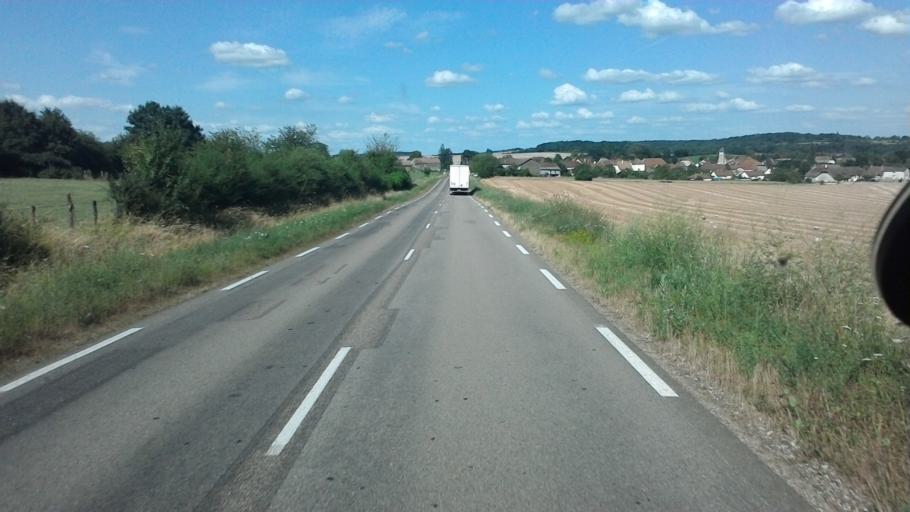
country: FR
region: Franche-Comte
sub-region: Departement de la Haute-Saone
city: Marnay
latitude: 47.3173
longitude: 5.6741
